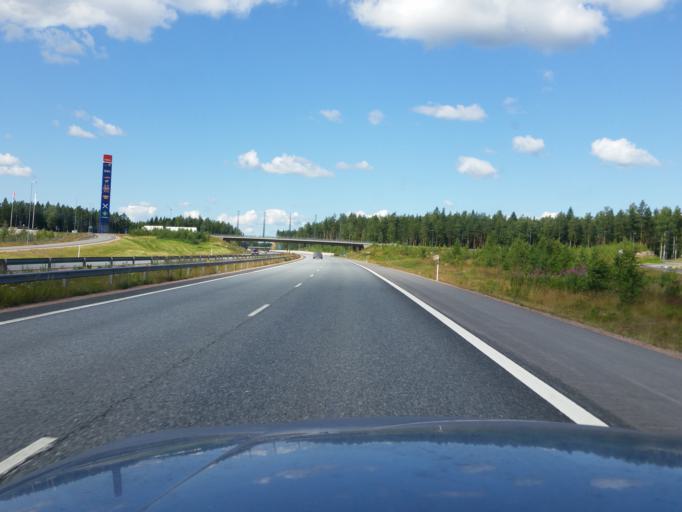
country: FI
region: Varsinais-Suomi
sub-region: Salo
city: Suomusjaervi
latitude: 60.3807
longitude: 23.6235
